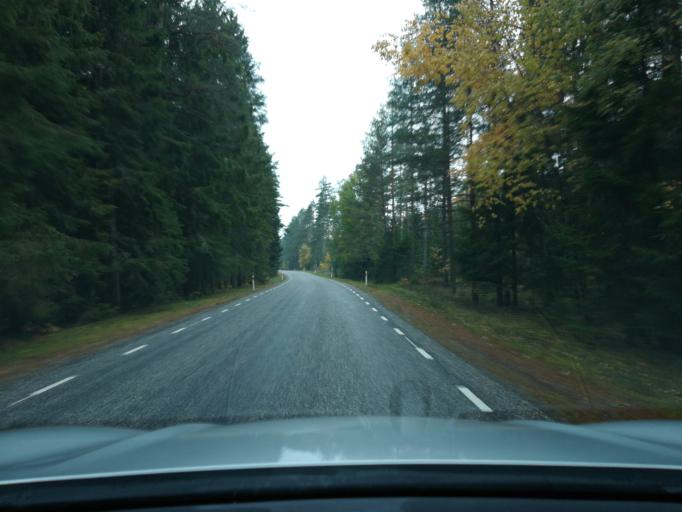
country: EE
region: Ida-Virumaa
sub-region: Johvi vald
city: Johvi
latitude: 59.1543
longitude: 27.3890
